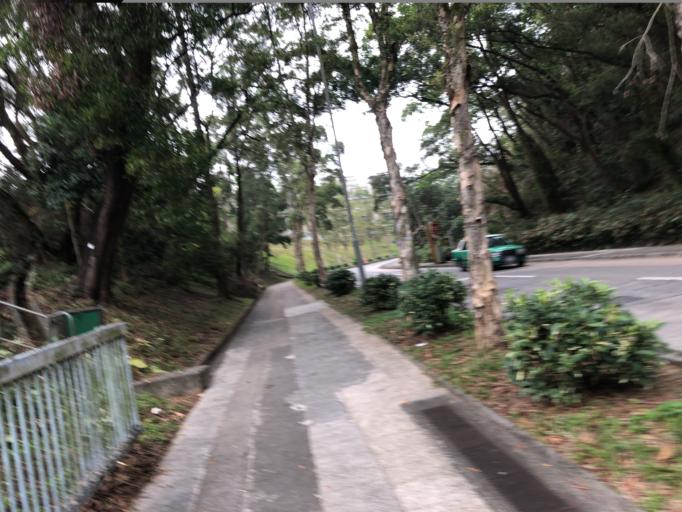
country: HK
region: Tai Po
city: Tai Po
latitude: 22.4644
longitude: 114.1930
